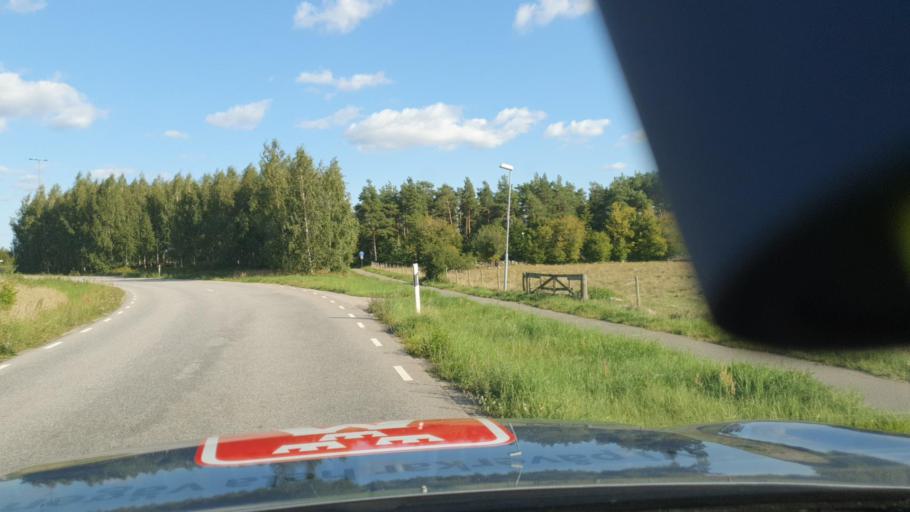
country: SE
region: Skane
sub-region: Bromolla Kommun
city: Bromoella
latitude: 56.0854
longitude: 14.4932
